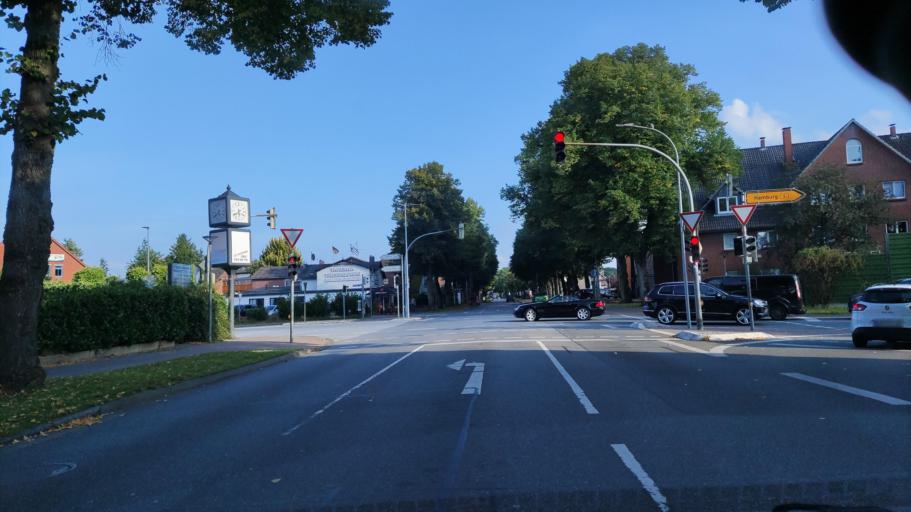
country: DE
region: Schleswig-Holstein
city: Bad Bramstedt
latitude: 53.9163
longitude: 9.8847
